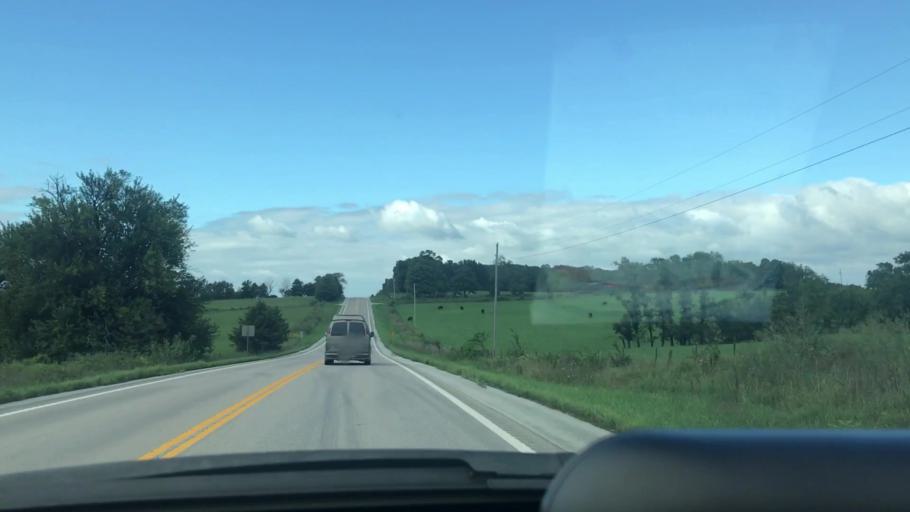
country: US
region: Missouri
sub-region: Hickory County
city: Hermitage
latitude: 37.9598
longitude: -93.2070
